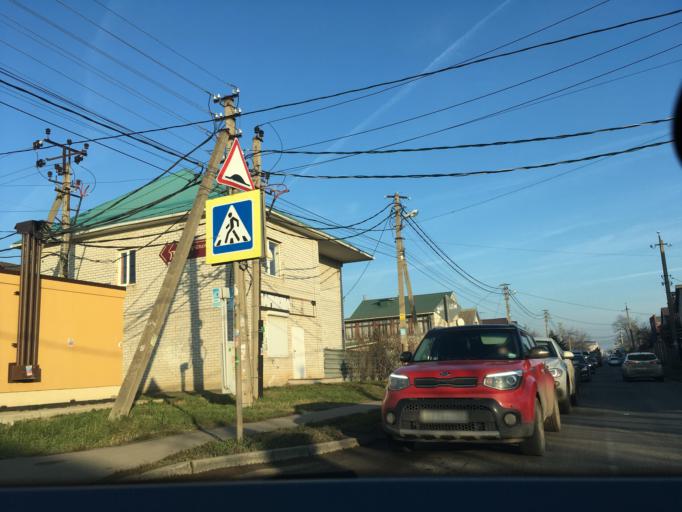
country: RU
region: Krasnodarskiy
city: Krasnodar
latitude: 45.1143
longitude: 39.0148
